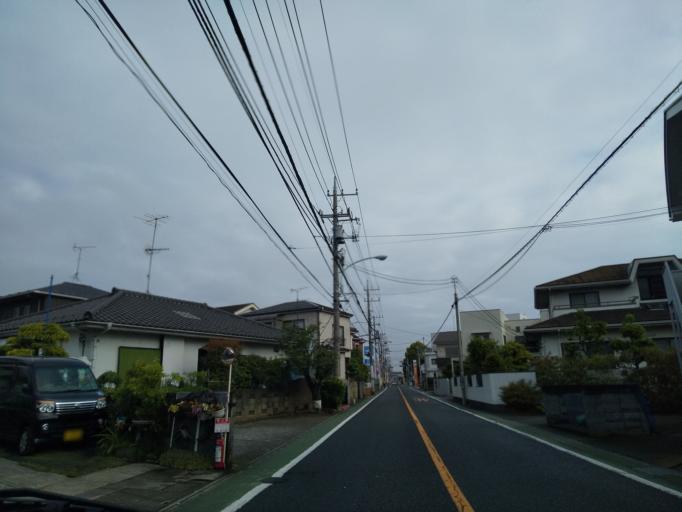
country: JP
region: Tokyo
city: Hino
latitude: 35.6700
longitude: 139.4042
